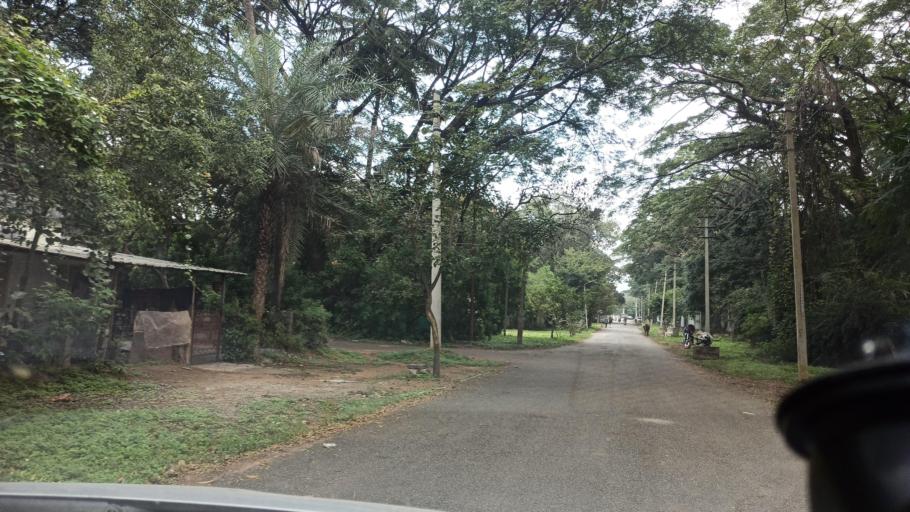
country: IN
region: Karnataka
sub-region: Bangalore Urban
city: Bangalore
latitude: 13.0066
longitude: 77.6810
